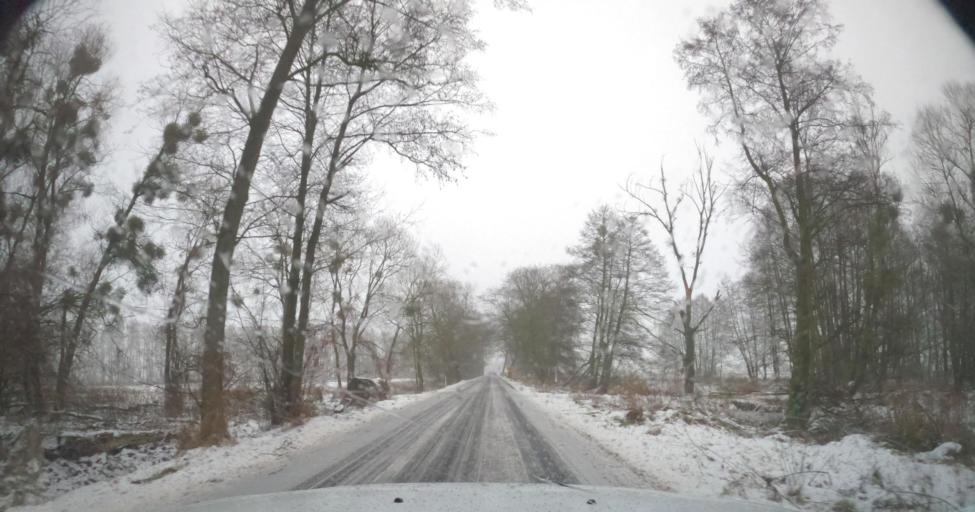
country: PL
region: West Pomeranian Voivodeship
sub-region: Powiat policki
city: Police
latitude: 53.5613
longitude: 14.6678
